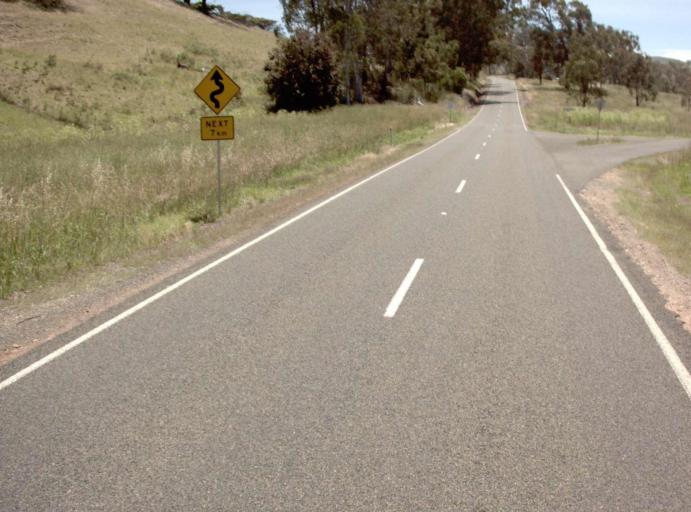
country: AU
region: Victoria
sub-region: East Gippsland
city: Bairnsdale
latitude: -37.4103
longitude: 147.8353
